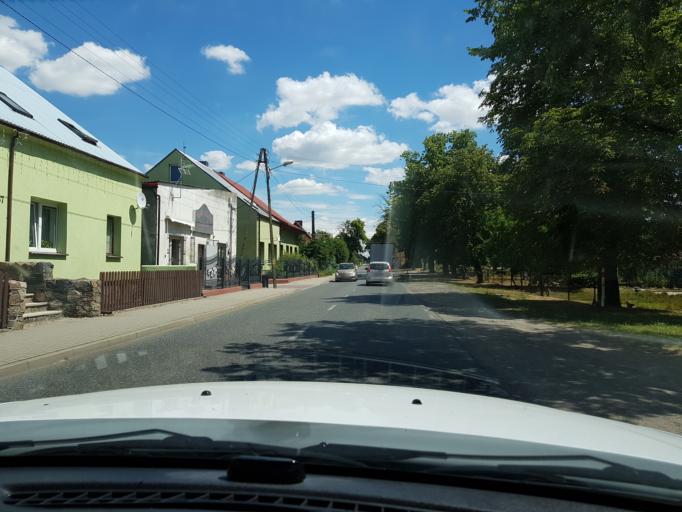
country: PL
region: West Pomeranian Voivodeship
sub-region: Powiat mysliborski
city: Nowogrodek Pomorski
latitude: 52.9083
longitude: 14.9551
